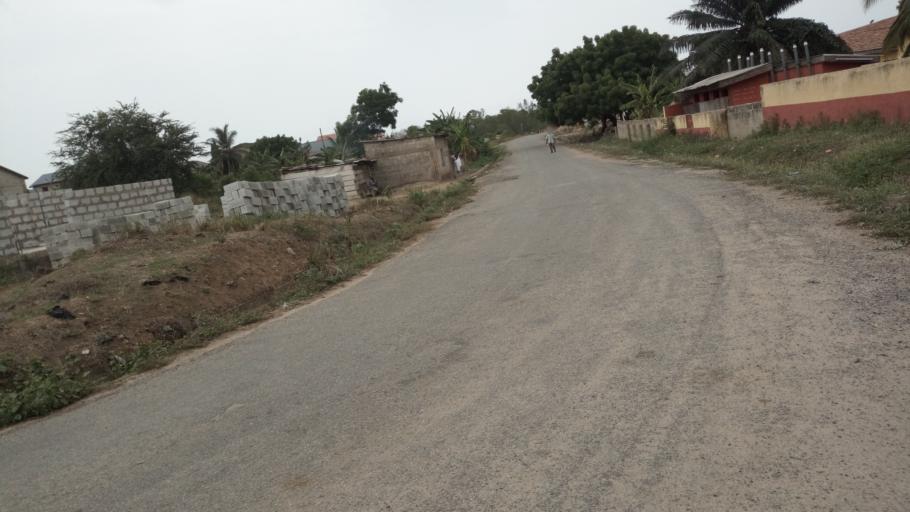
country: GH
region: Central
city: Winneba
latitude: 5.3815
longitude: -0.6405
